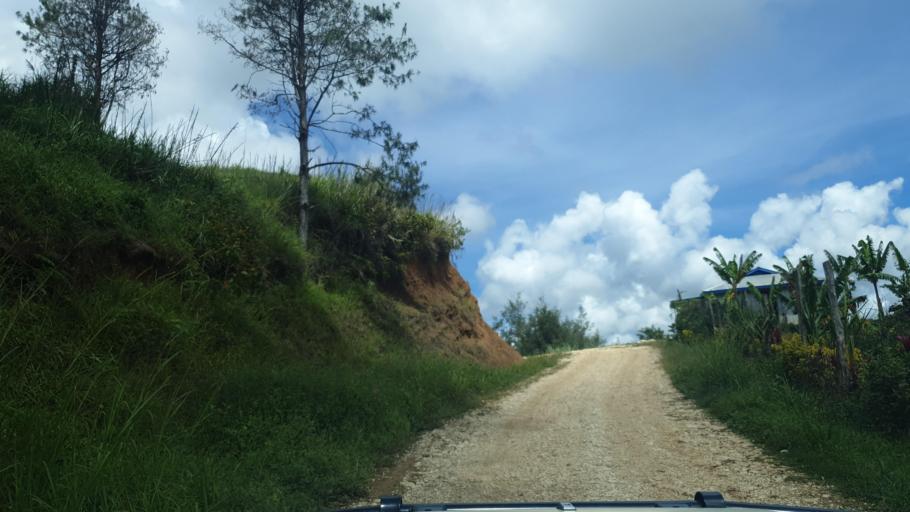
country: PG
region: Chimbu
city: Kundiawa
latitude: -6.2152
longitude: 145.1372
